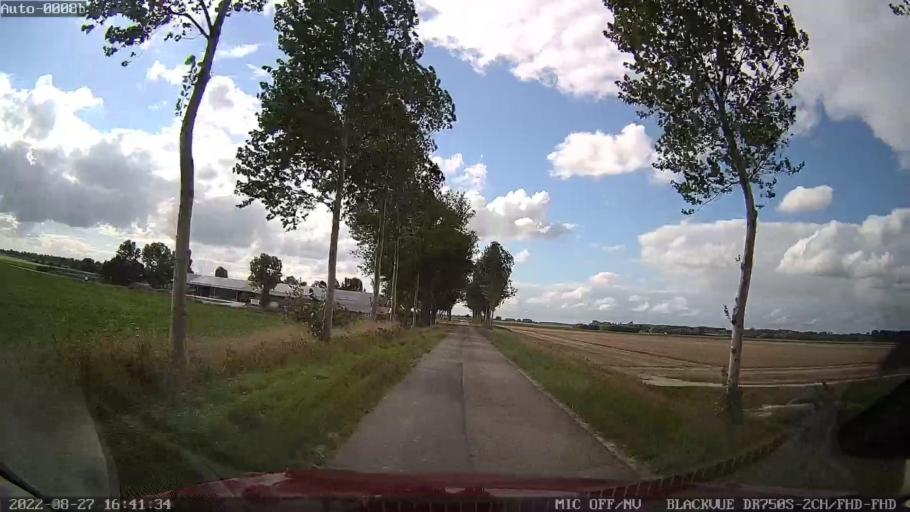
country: NL
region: Zeeland
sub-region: Schouwen-Duiveland
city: Bruinisse
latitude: 51.6657
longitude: 3.9595
